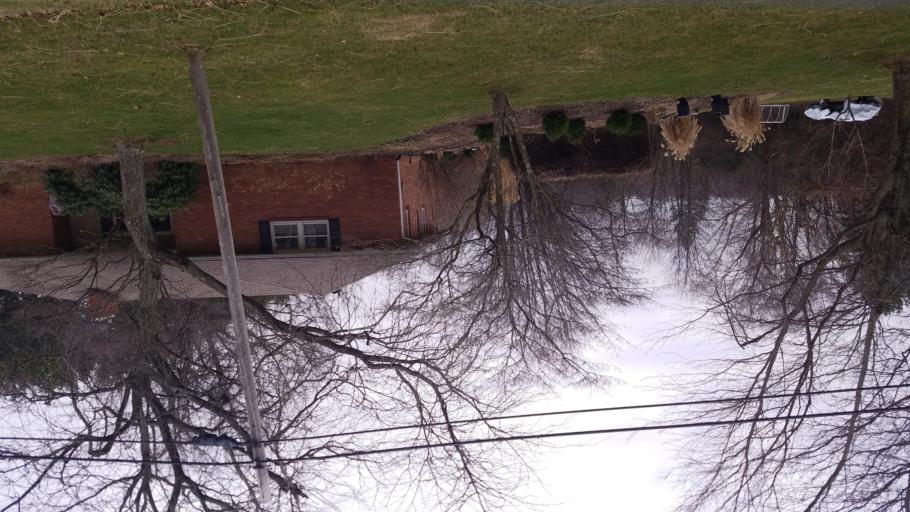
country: US
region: Ohio
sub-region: Sandusky County
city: Bellville
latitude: 40.6493
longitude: -82.5098
